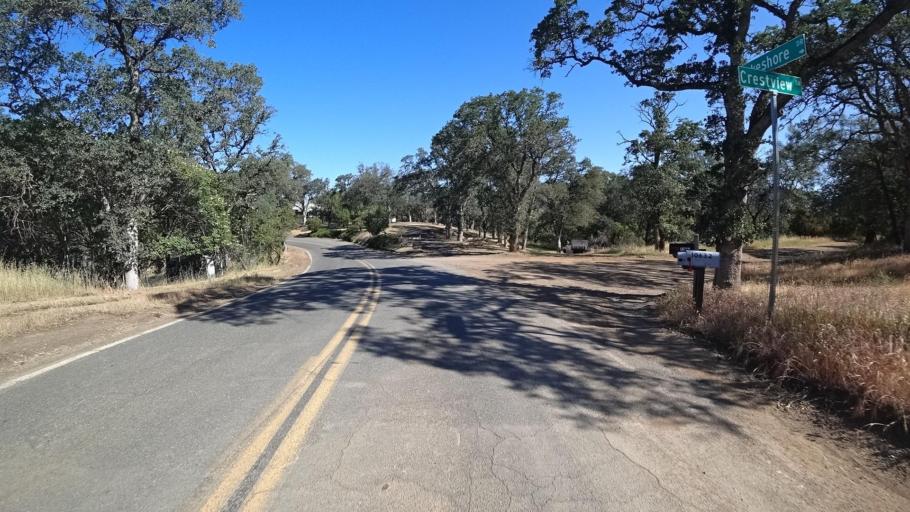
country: US
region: California
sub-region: Lake County
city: Clearlake Oaks
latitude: 39.0030
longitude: -122.7132
